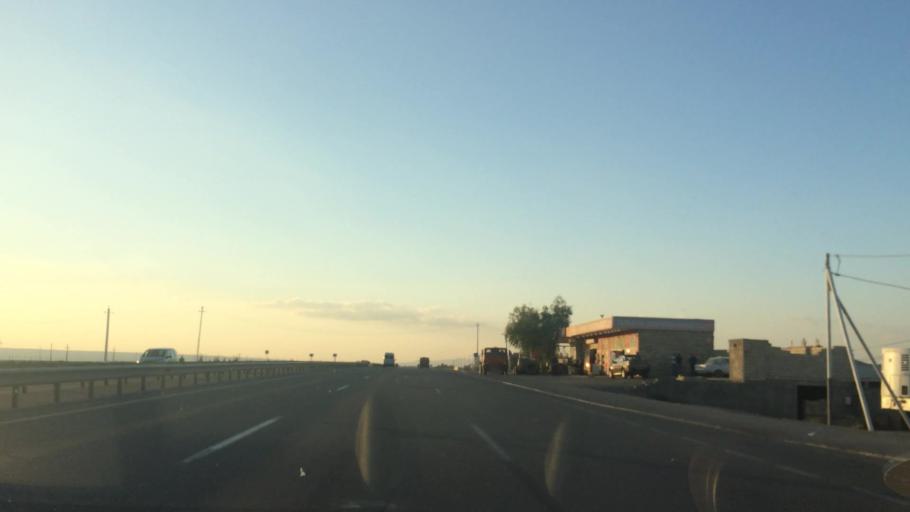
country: AZ
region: Baki
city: Qobustan
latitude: 39.9729
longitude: 49.2575
